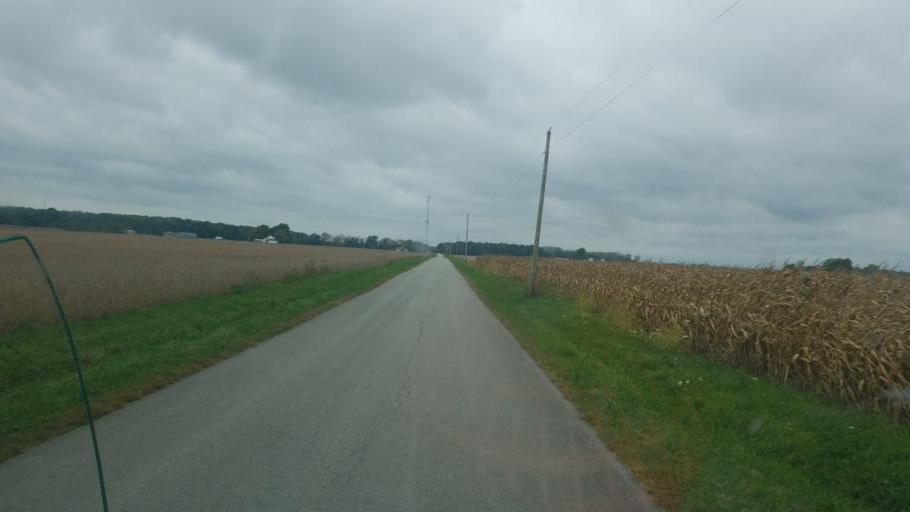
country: US
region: Ohio
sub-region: Seneca County
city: Fostoria
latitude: 41.0792
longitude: -83.5054
